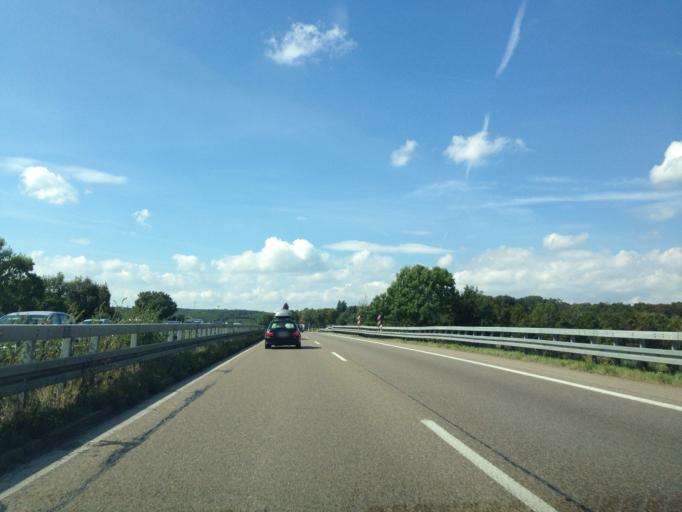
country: DE
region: Baden-Wuerttemberg
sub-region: Regierungsbezirk Stuttgart
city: Hohenstadt
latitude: 48.5325
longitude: 9.6703
